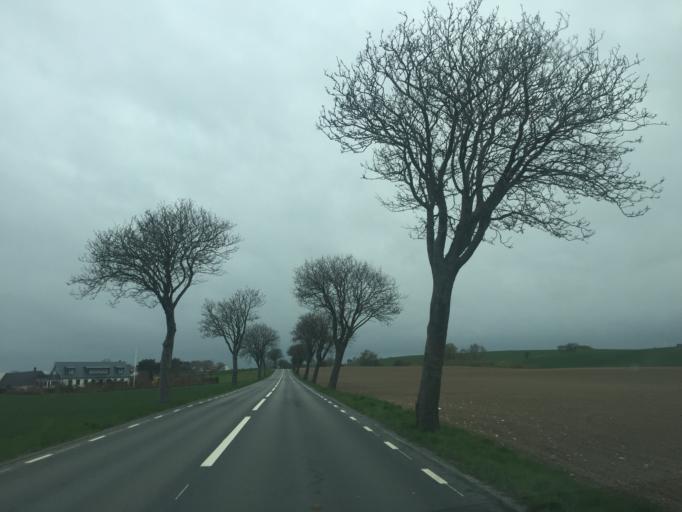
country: SE
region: Skane
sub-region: Skurups Kommun
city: Skivarp
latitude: 55.4194
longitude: 13.6300
